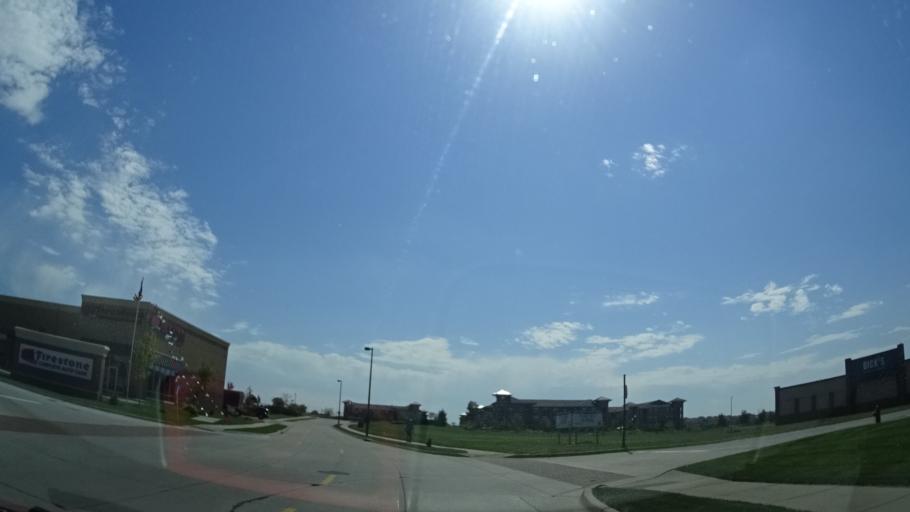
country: US
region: Nebraska
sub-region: Sarpy County
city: Papillion
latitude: 41.1341
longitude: -96.0250
